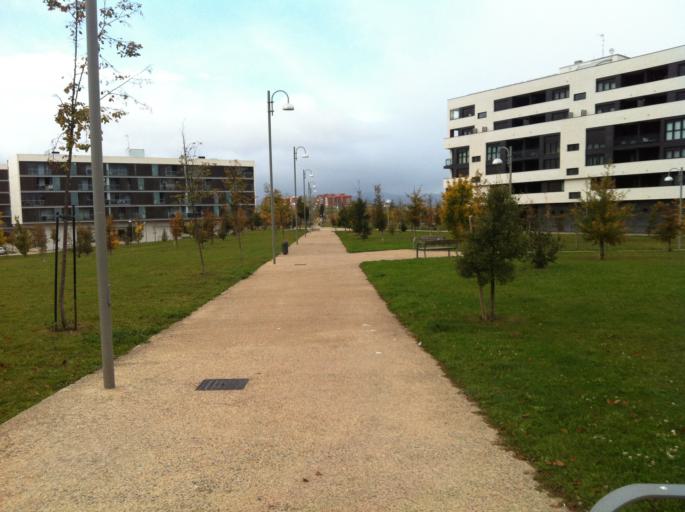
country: ES
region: Basque Country
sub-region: Provincia de Alava
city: Gasteiz / Vitoria
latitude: 42.8490
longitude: -2.6959
